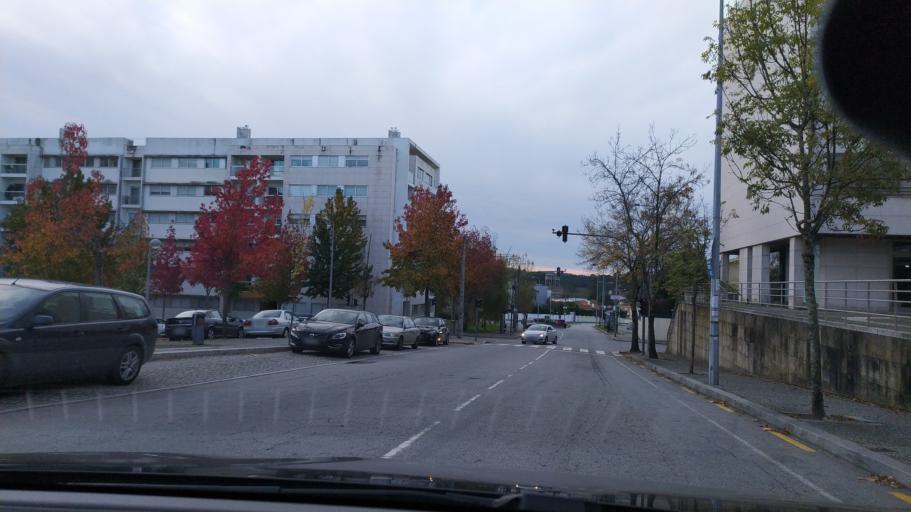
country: PT
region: Porto
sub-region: Maia
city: Maia
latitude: 41.2391
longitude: -8.6481
